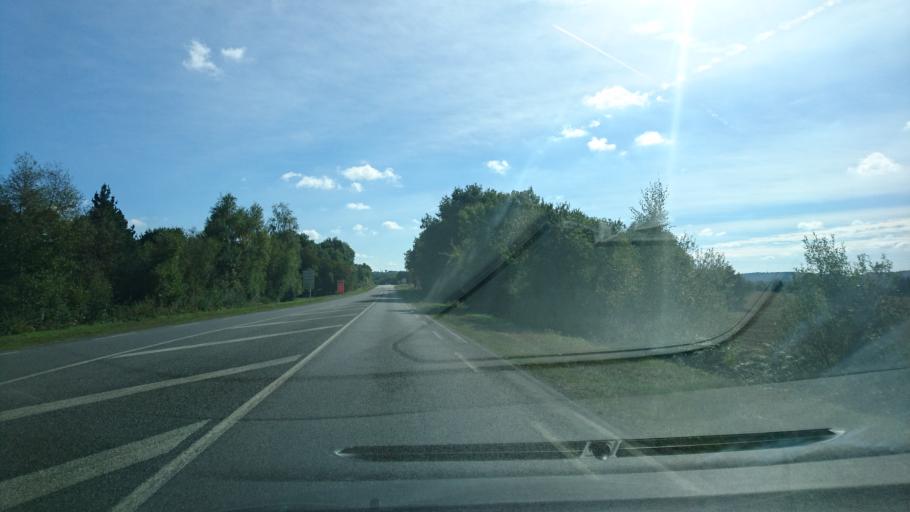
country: FR
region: Brittany
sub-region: Departement du Morbihan
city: Saint-Perreux
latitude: 47.6797
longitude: -2.1306
